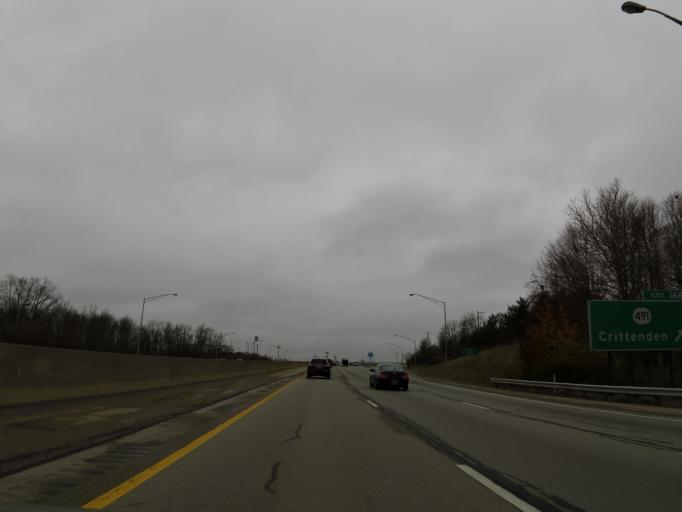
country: US
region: Kentucky
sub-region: Grant County
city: Crittenden
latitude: 38.7931
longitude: -84.6043
